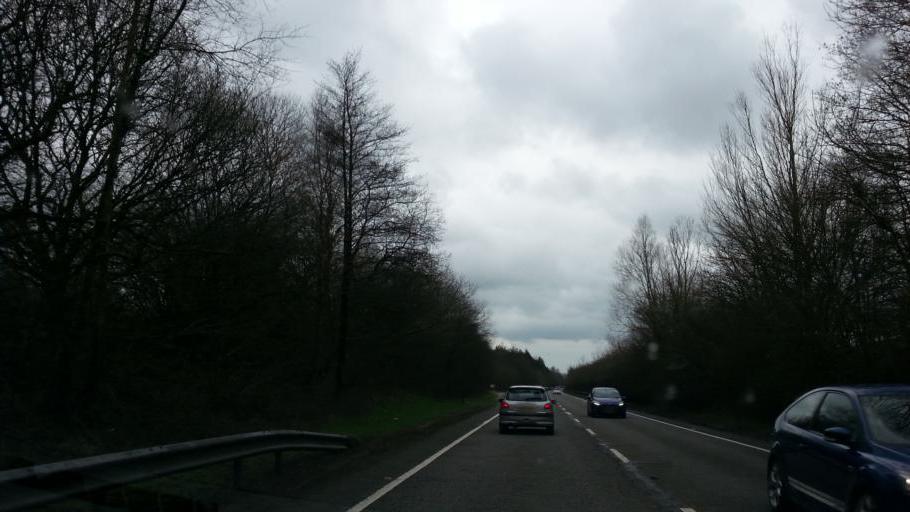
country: GB
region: England
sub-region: Devon
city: South Molton
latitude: 51.0497
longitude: -3.9300
